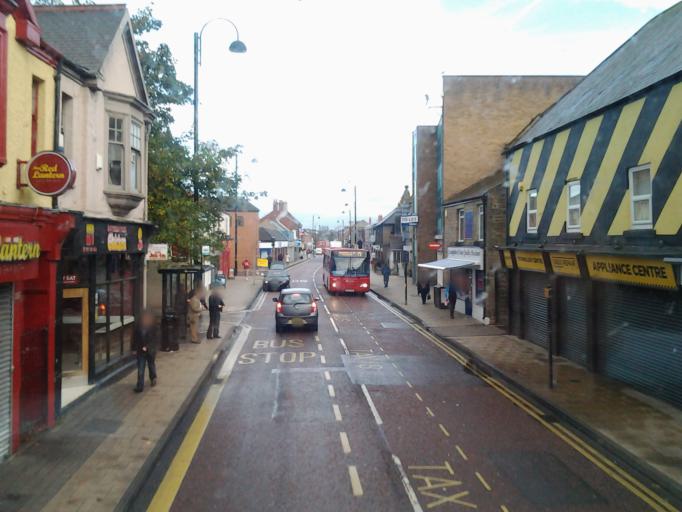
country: GB
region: England
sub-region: County Durham
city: Chester-le-Street
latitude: 54.8526
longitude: -1.5733
